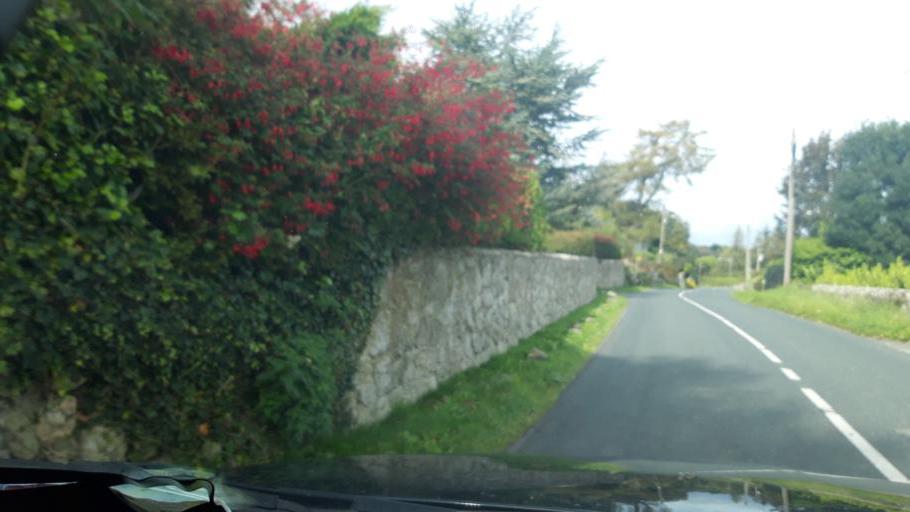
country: IE
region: Leinster
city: Sandyford
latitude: 53.2378
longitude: -6.2221
